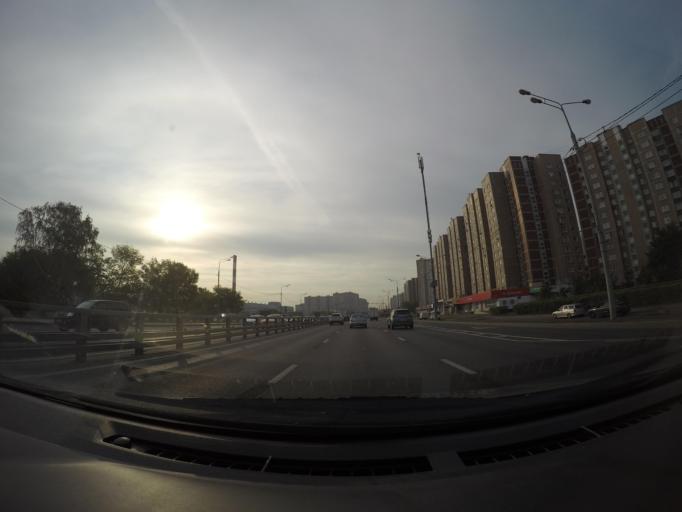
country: RU
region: Moscow
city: Zhulebino
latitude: 55.7036
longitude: 37.8472
